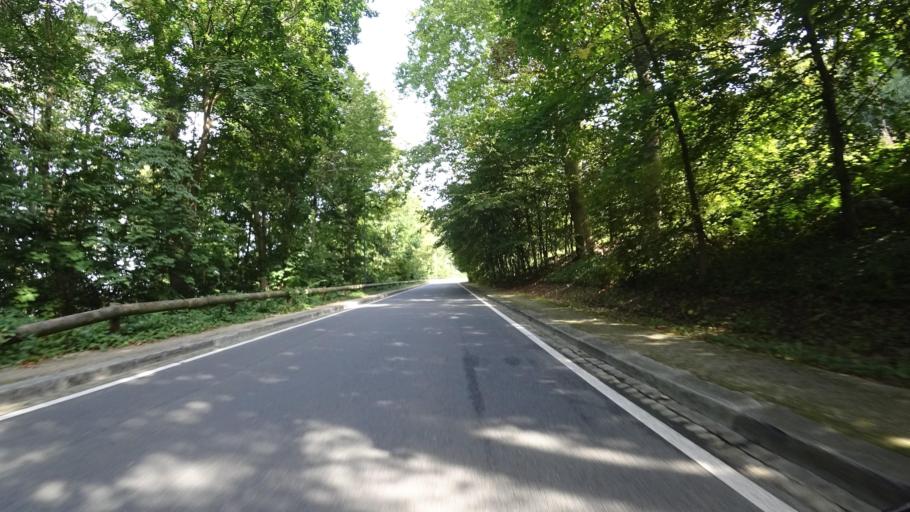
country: BE
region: Wallonia
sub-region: Province de Namur
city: Namur
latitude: 50.4611
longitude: 4.8522
